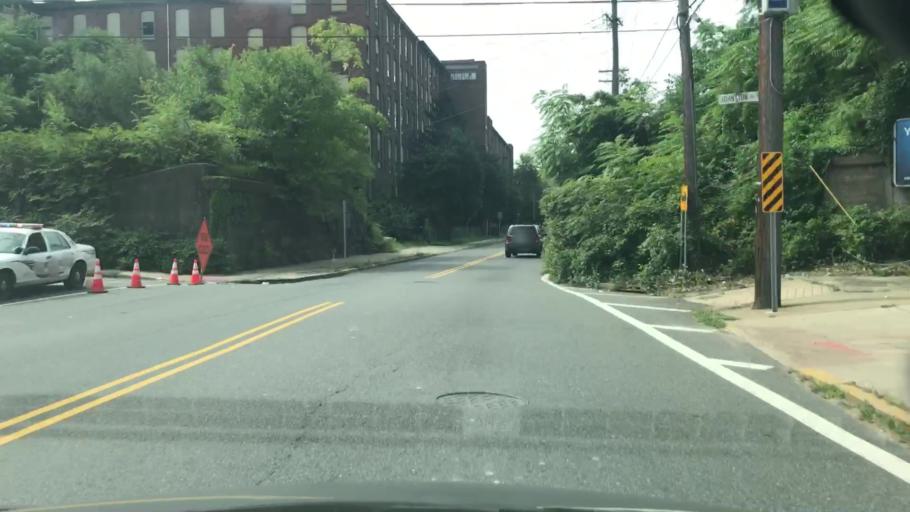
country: US
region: New Jersey
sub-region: Hudson County
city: East Newark
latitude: 40.7539
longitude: -74.1629
